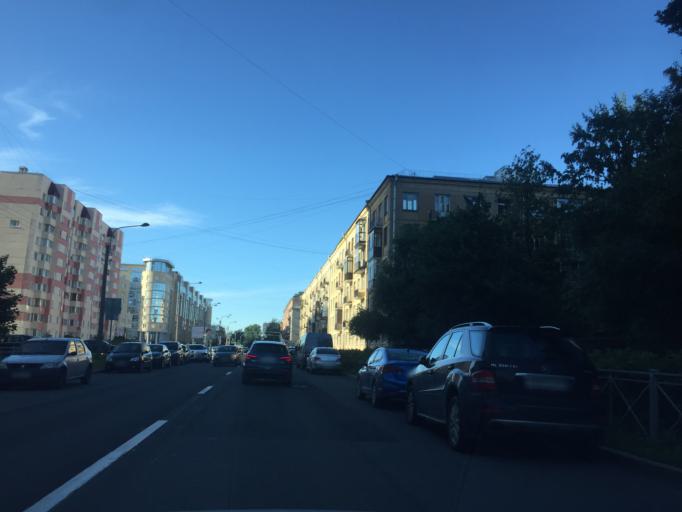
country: RU
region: St.-Petersburg
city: Admiralteisky
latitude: 59.8738
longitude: 30.3136
